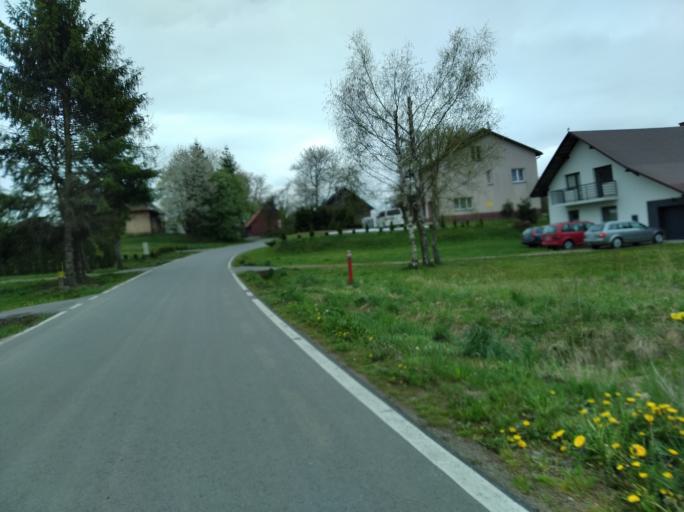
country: PL
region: Subcarpathian Voivodeship
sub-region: Powiat brzozowski
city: Blizne
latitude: 49.7404
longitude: 21.9849
